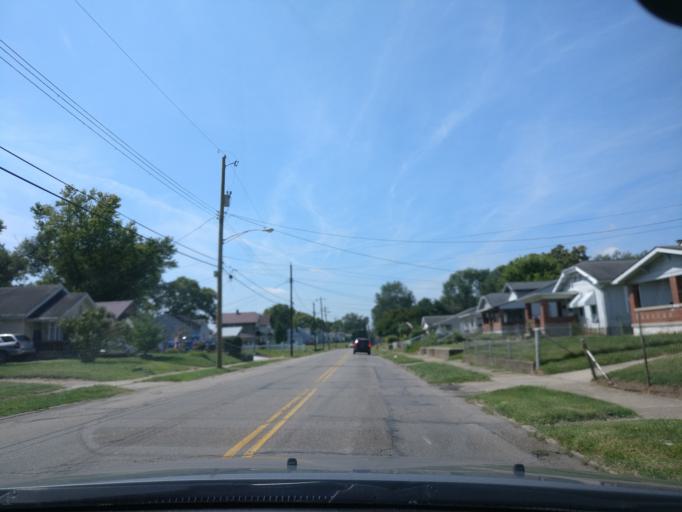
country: US
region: Ohio
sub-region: Butler County
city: Middletown
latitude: 39.4934
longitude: -84.4067
